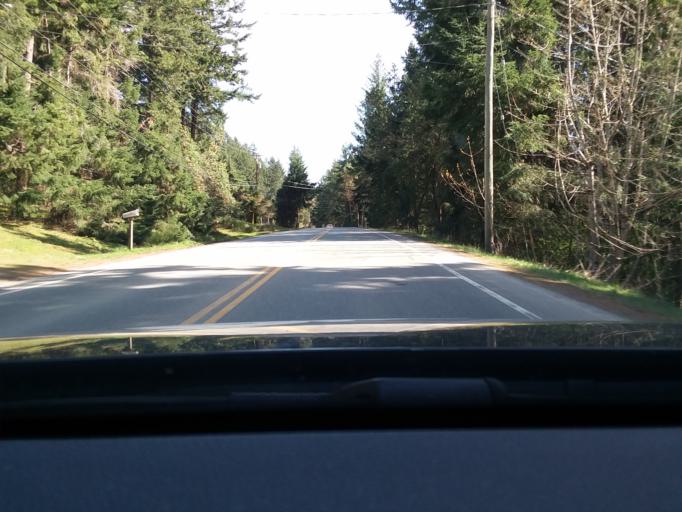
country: CA
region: British Columbia
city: North Saanich
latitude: 48.8583
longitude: -123.4830
